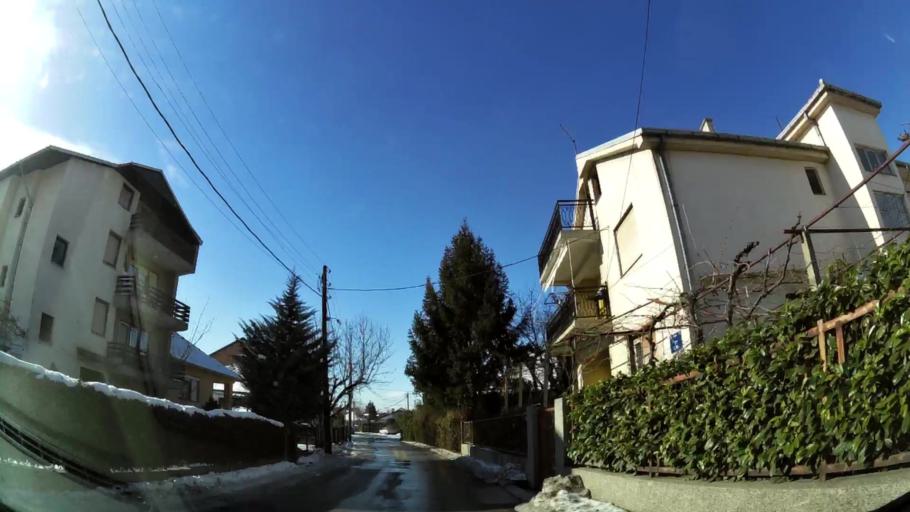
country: MK
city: Krushopek
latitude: 42.0039
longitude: 21.3563
